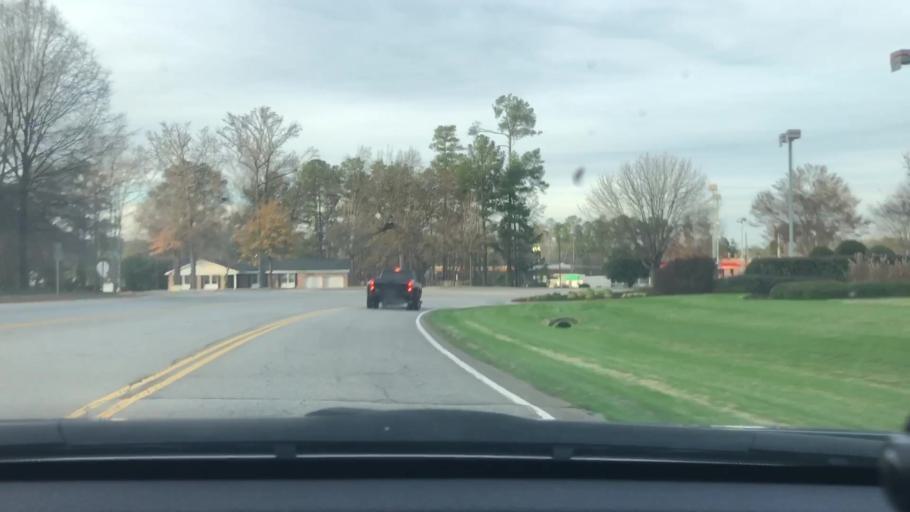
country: US
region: South Carolina
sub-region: Lexington County
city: Irmo
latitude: 34.0983
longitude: -81.1784
